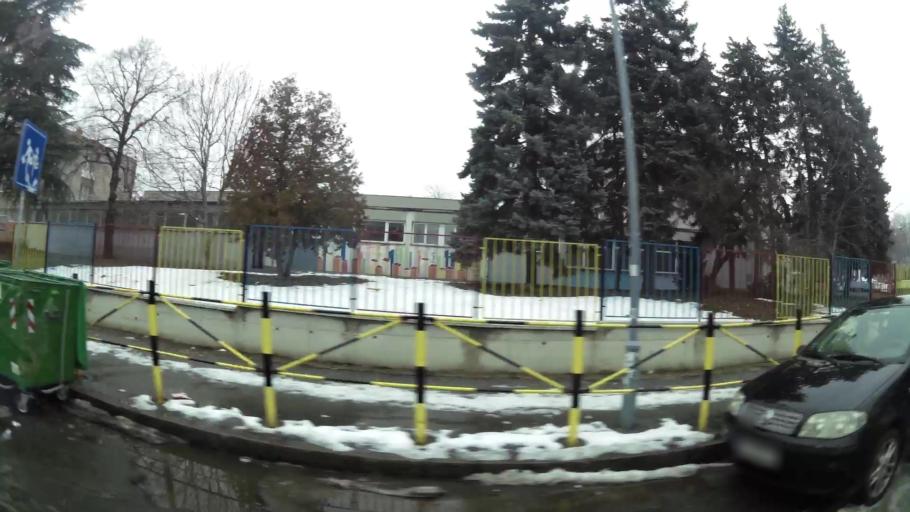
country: RS
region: Central Serbia
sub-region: Belgrade
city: Vozdovac
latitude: 44.7700
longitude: 20.4907
